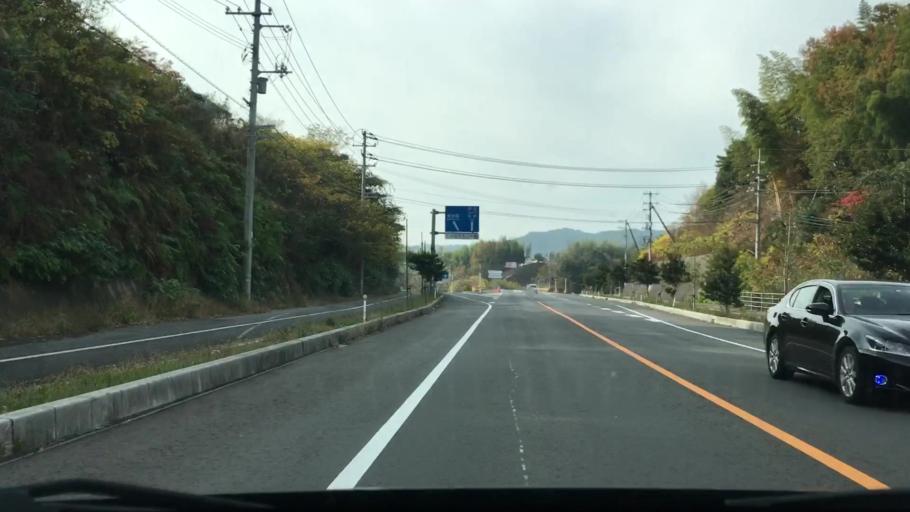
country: JP
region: Yamaguchi
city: Iwakuni
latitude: 34.1537
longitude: 132.1896
